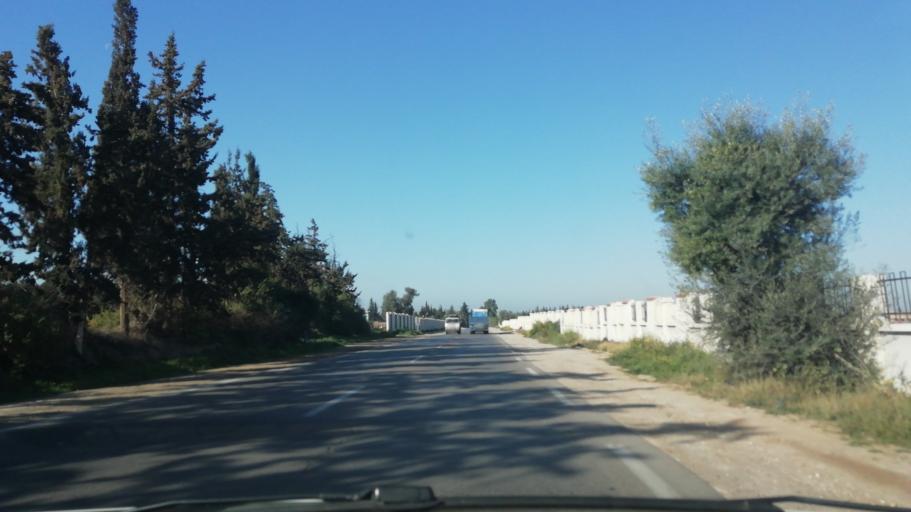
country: DZ
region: Mascara
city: Sig
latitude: 35.5770
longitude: 0.0022
